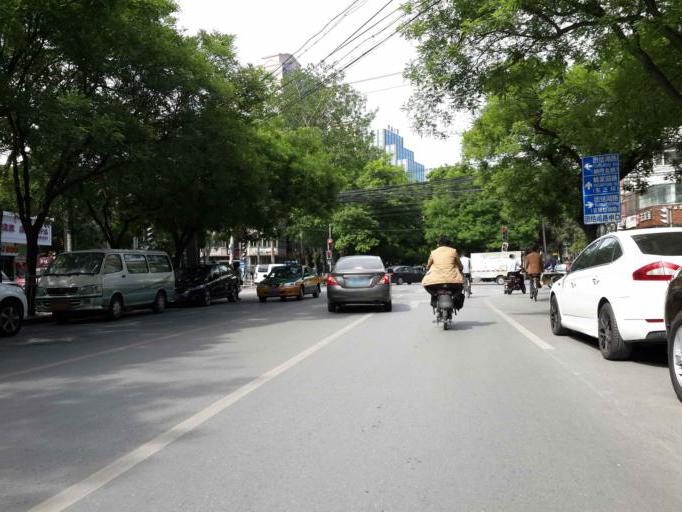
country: CN
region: Beijing
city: Chaowai
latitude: 39.9283
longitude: 116.4613
